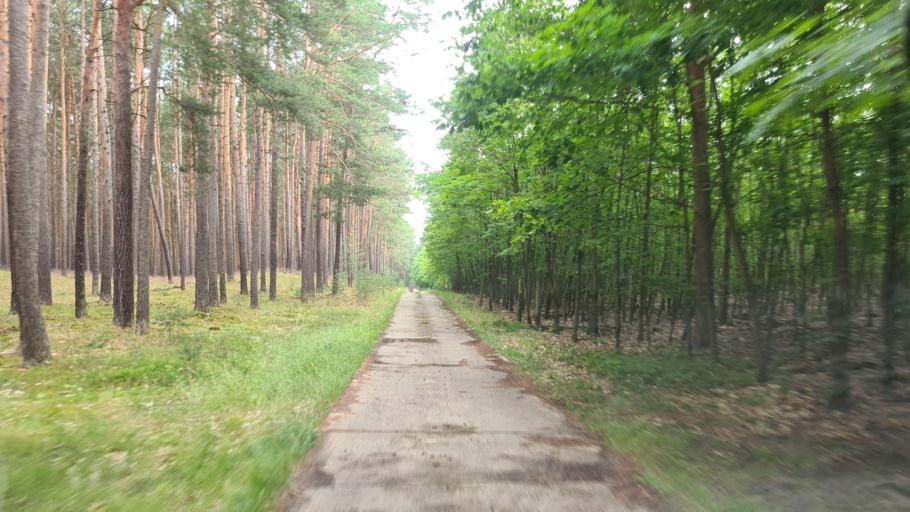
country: DE
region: Brandenburg
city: Crinitz
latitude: 51.7185
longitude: 13.7153
